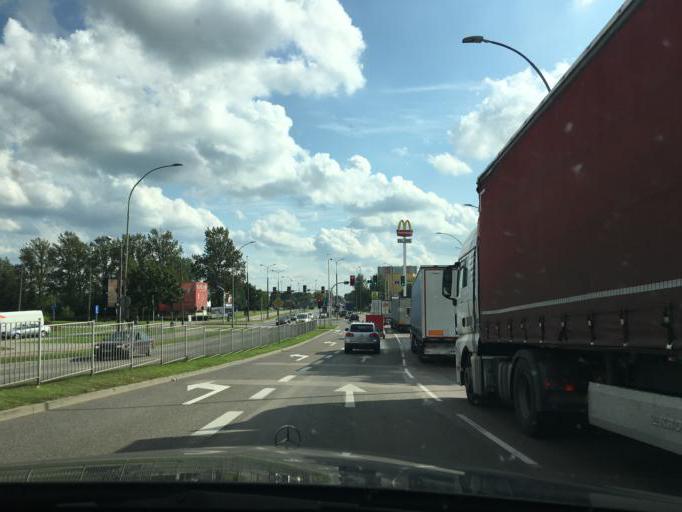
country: PL
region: Podlasie
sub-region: Suwalki
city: Suwalki
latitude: 54.1085
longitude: 22.9356
